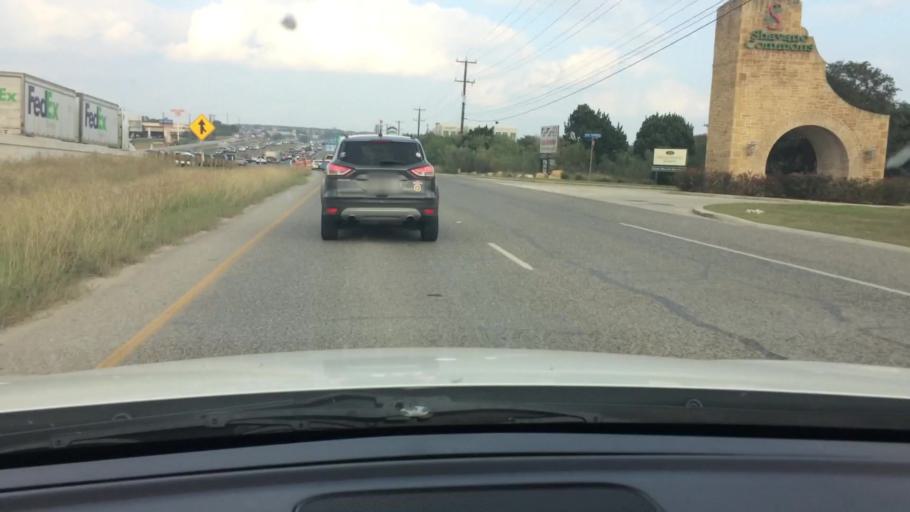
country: US
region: Texas
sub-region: Bexar County
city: Shavano Park
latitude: 29.5948
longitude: -98.5759
